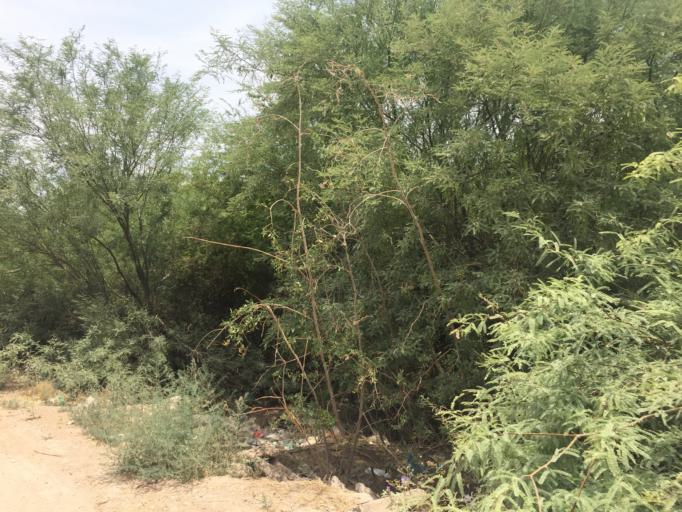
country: MX
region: Durango
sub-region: Gomez Palacio
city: San Jose de Vinedo
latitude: 25.6735
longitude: -103.4394
